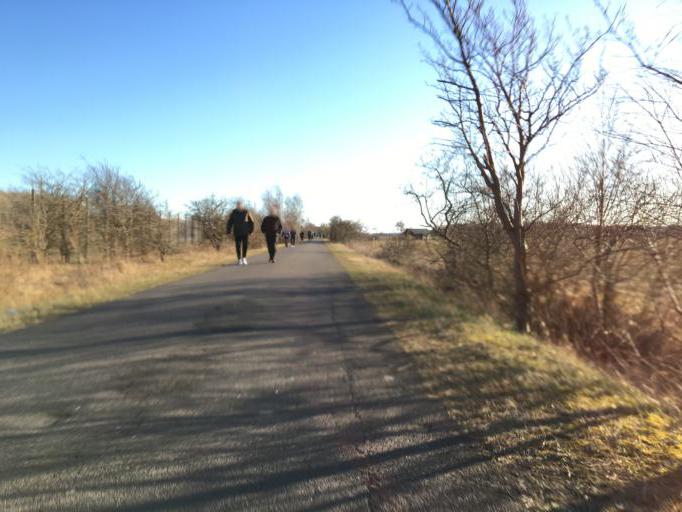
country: DK
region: Capital Region
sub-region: Tarnby Kommune
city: Tarnby
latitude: 55.5998
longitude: 12.5737
